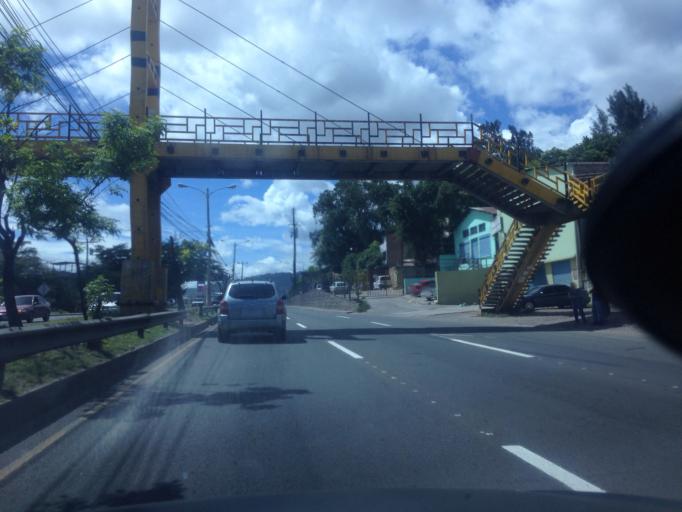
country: HN
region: Francisco Morazan
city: Tegucigalpa
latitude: 14.0748
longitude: -87.1663
